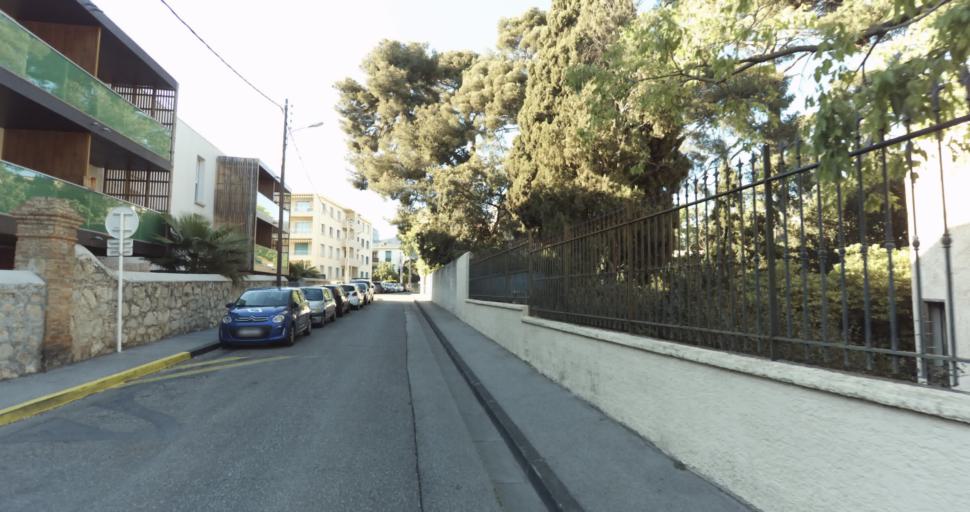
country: FR
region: Provence-Alpes-Cote d'Azur
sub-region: Departement du Var
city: Toulon
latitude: 43.1337
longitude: 5.9084
